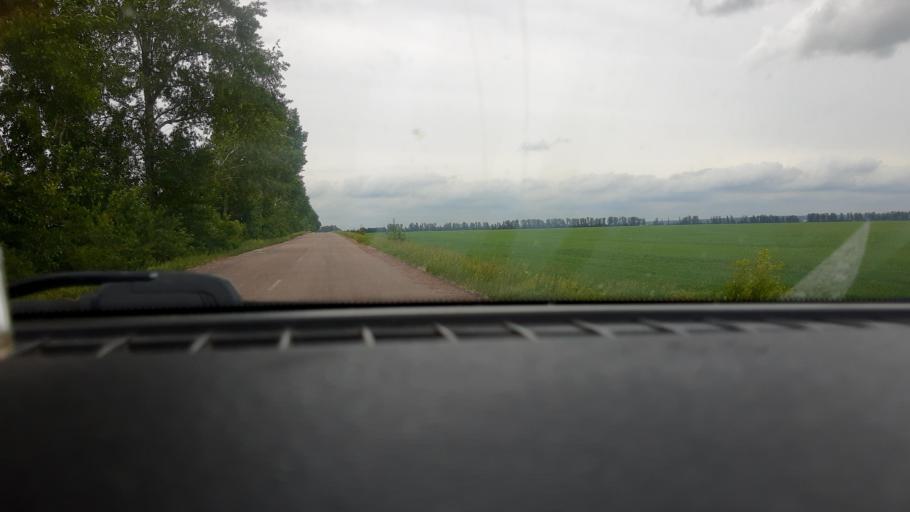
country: RU
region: Bashkortostan
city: Asanovo
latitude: 54.7465
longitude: 55.4992
